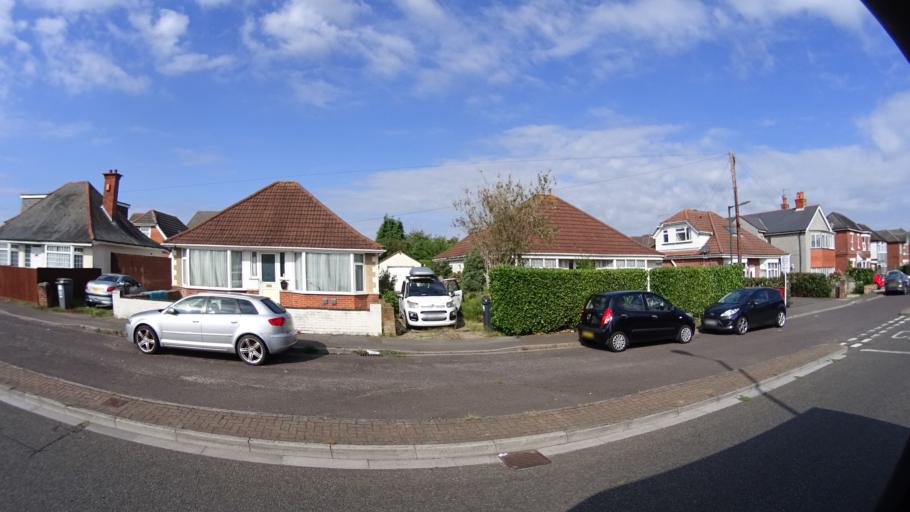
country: GB
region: England
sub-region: Bournemouth
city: Bournemouth
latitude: 50.7492
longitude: -1.8870
